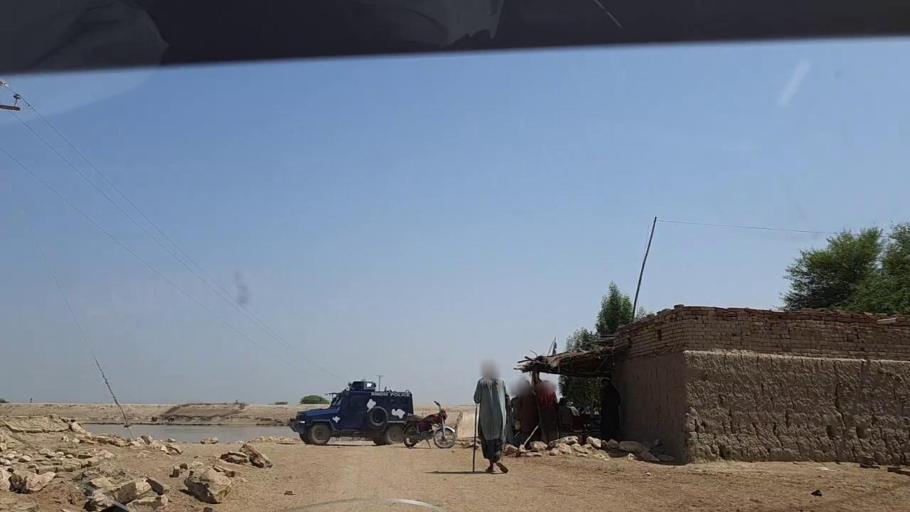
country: PK
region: Sindh
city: Ghauspur
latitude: 28.1343
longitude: 69.0859
